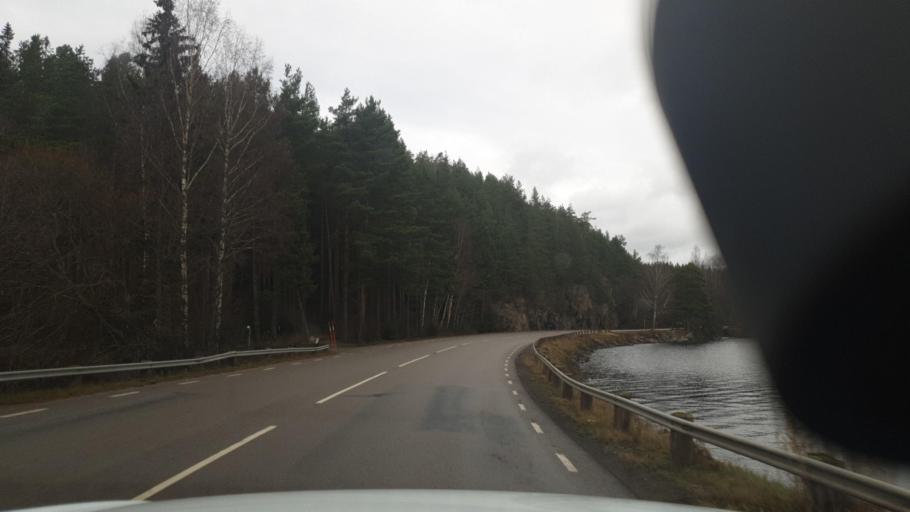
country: SE
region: Vaermland
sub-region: Arvika Kommun
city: Arvika
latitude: 59.7178
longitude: 12.6278
